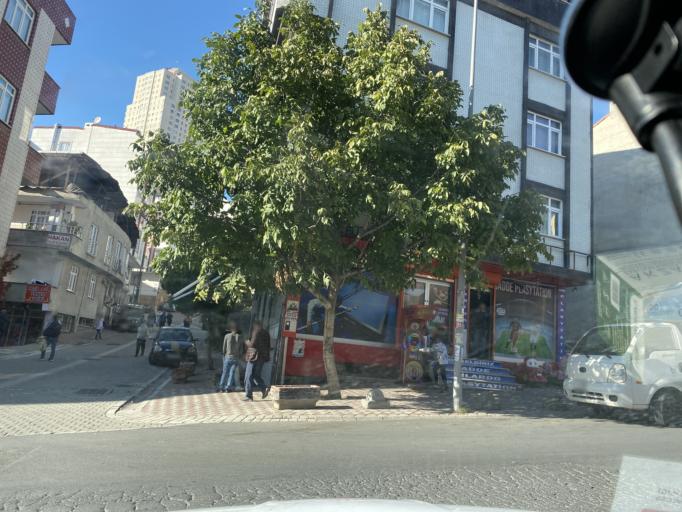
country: TR
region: Istanbul
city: Esenyurt
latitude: 41.0310
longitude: 28.6528
